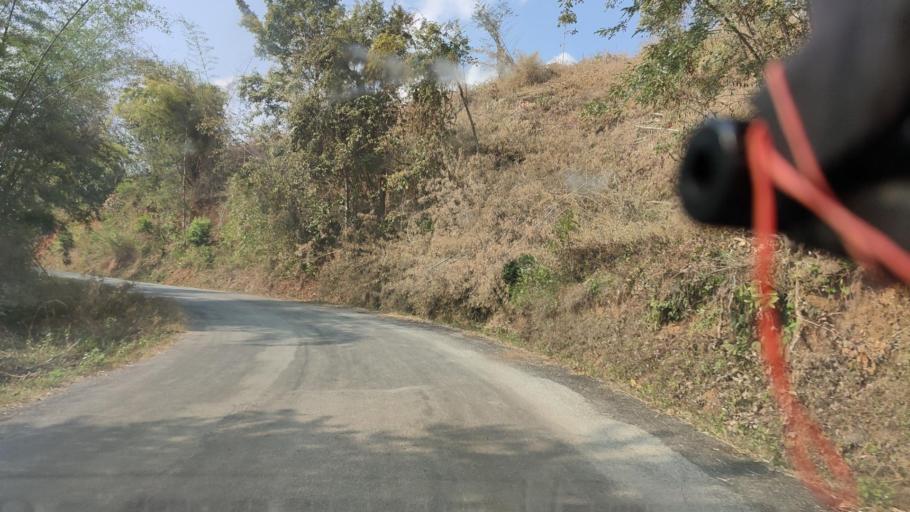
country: CN
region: Yunnan
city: Nayun
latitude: 21.4387
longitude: 99.6295
